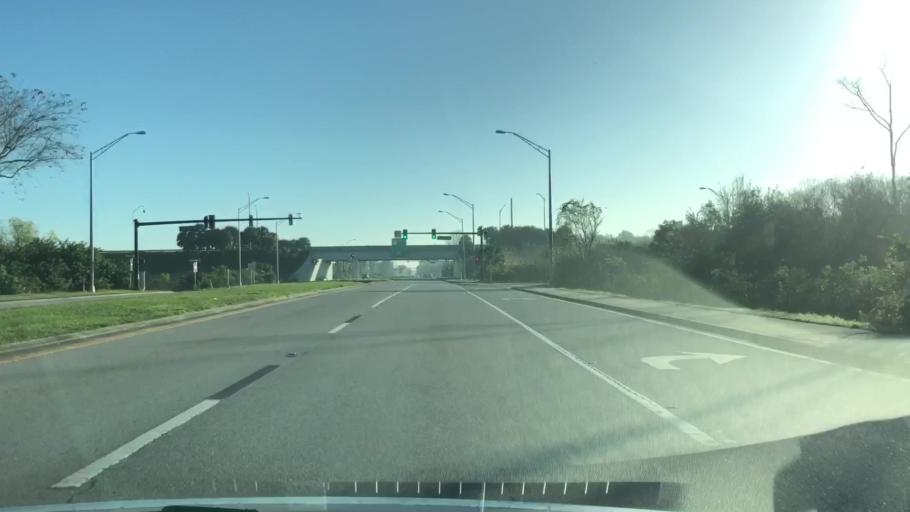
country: US
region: Florida
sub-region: Seminole County
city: Lake Mary
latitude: 28.7864
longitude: -81.3036
